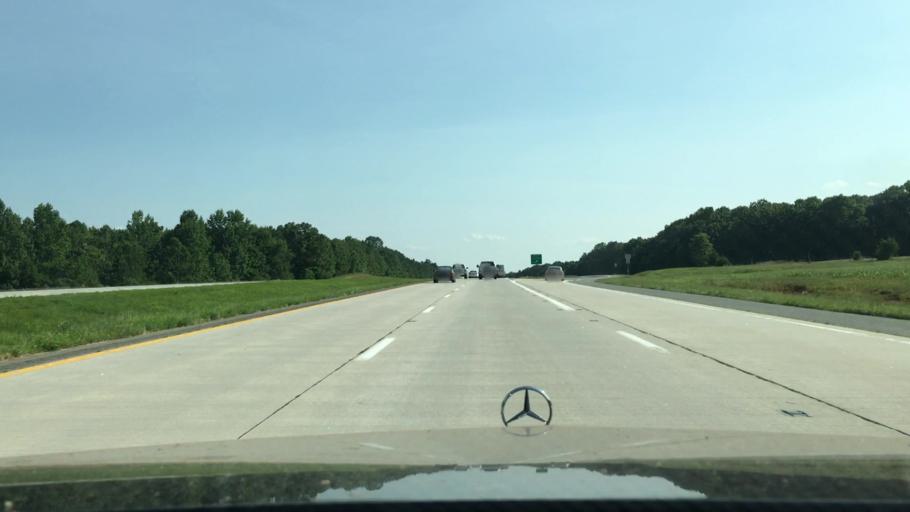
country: US
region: Virginia
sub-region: Amherst County
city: Madison Heights
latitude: 37.4940
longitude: -79.0706
